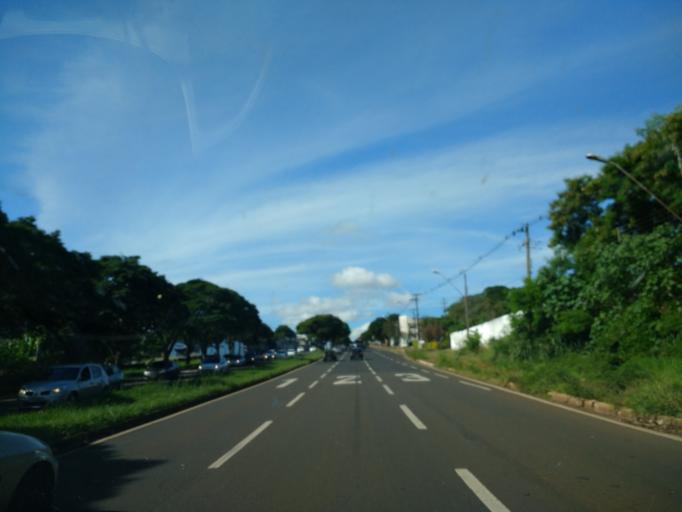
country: BR
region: Parana
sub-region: Maringa
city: Maringa
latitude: -23.4182
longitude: -51.9614
